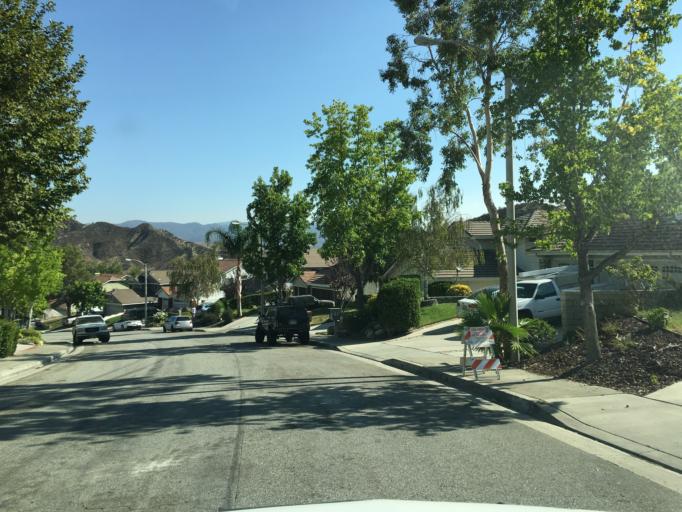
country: US
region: California
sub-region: Los Angeles County
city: Castaic
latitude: 34.4846
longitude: -118.6349
